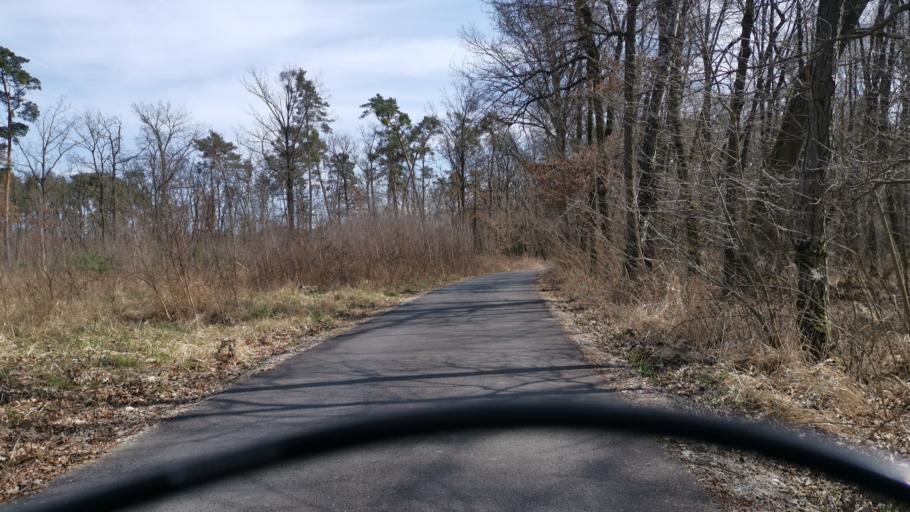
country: SK
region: Trnavsky
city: Gbely
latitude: 48.7075
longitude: 17.0730
